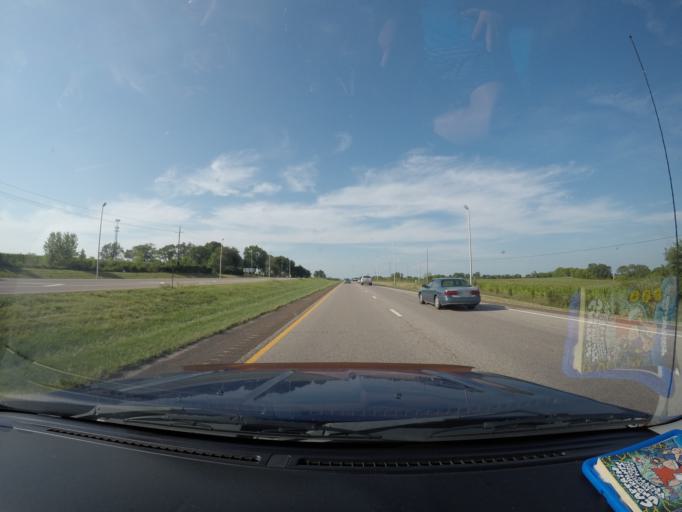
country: US
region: Kansas
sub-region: Leavenworth County
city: Basehor
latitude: 39.1876
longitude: -94.9003
